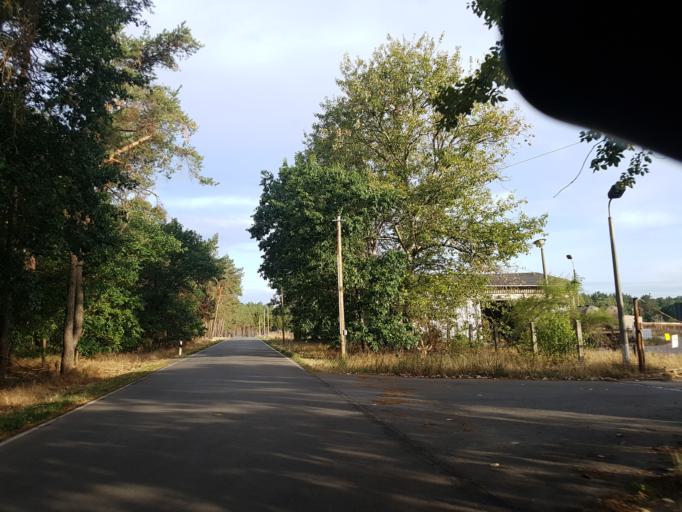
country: DE
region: Saxony-Anhalt
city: Holzdorf
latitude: 51.8000
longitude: 13.0913
